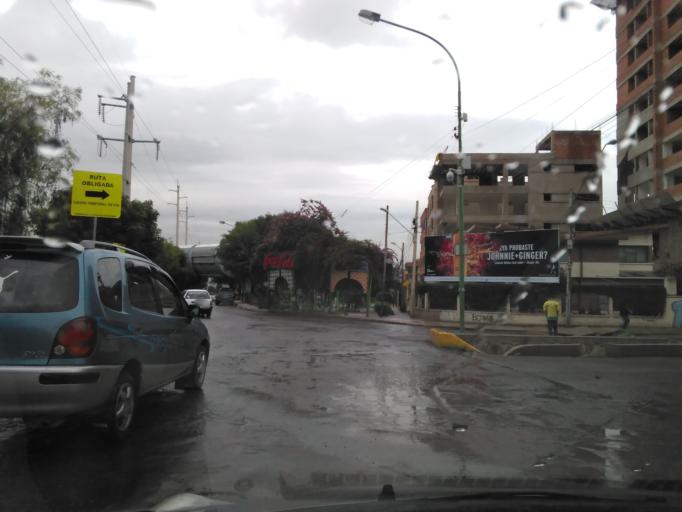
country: BO
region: Cochabamba
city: Cochabamba
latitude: -17.3785
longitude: -66.1496
